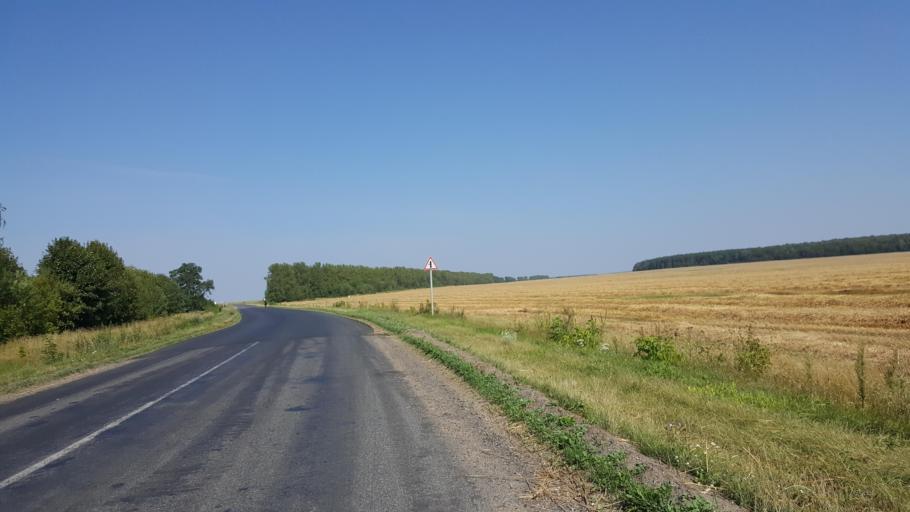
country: BY
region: Brest
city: Kamyanyets
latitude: 52.4414
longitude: 23.7425
